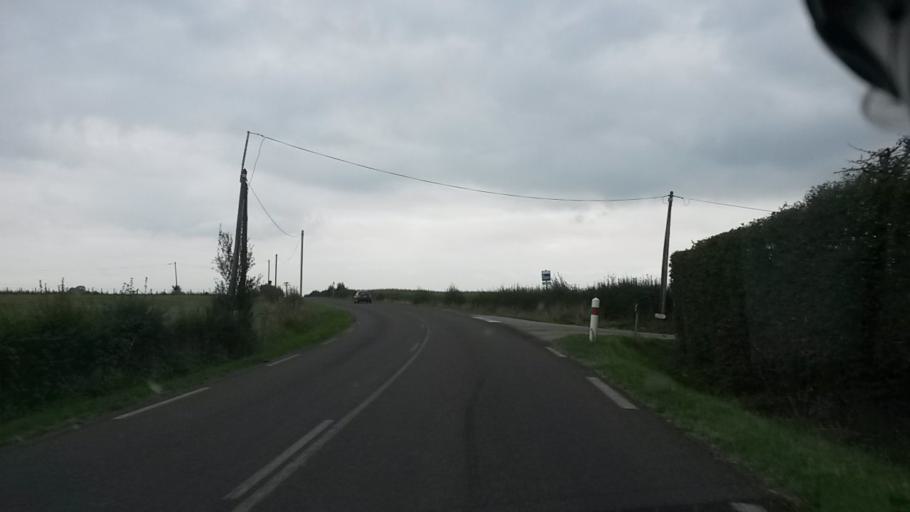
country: FR
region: Haute-Normandie
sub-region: Departement de la Seine-Maritime
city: Gaillefontaine
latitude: 49.6387
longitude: 1.6071
